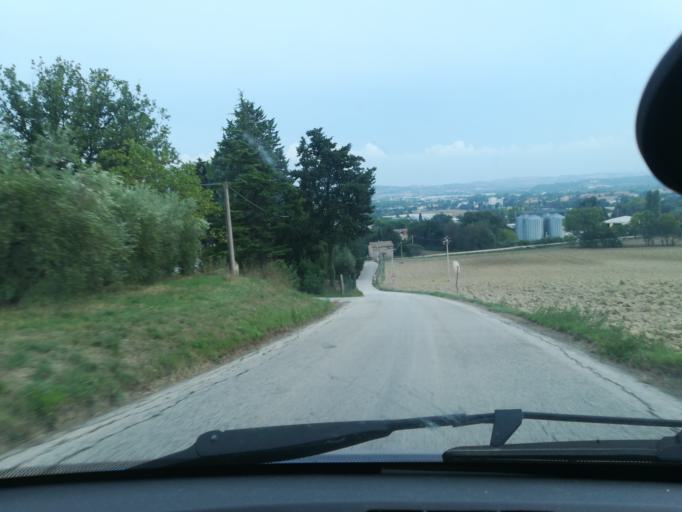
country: IT
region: The Marches
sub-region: Provincia di Macerata
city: Piediripa
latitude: 43.2883
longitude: 13.4880
